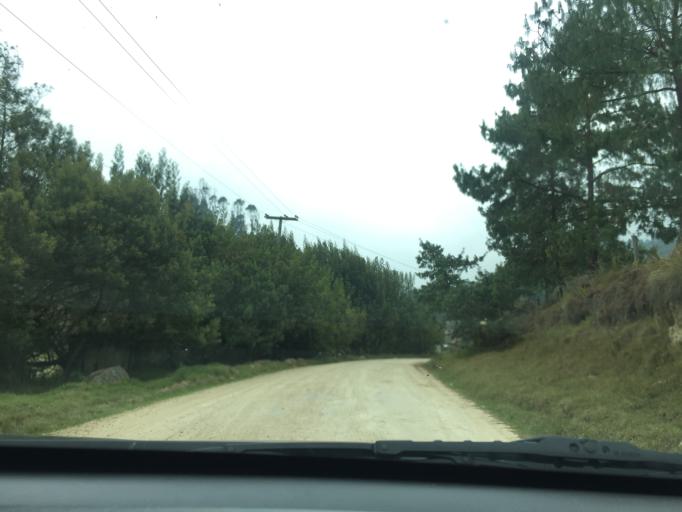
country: CO
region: Cundinamarca
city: Bojaca
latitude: 4.6861
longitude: -74.3181
